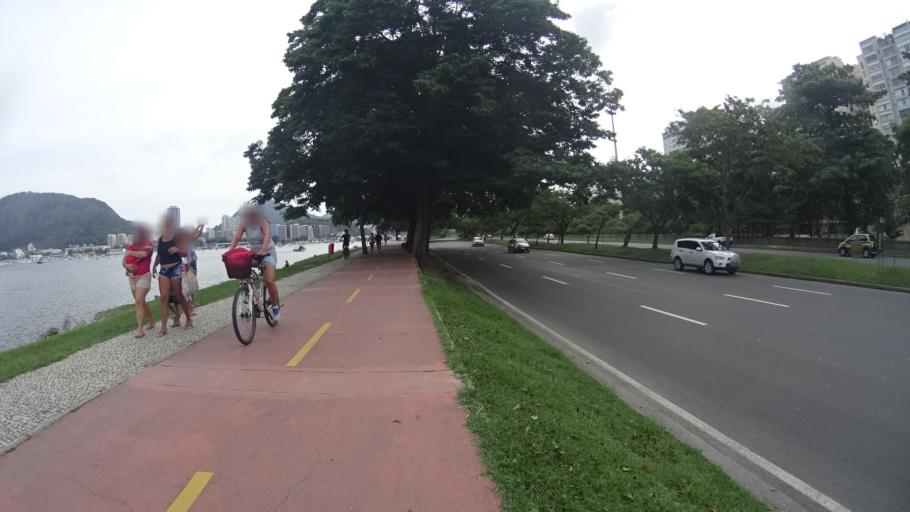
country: BR
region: Rio de Janeiro
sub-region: Rio De Janeiro
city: Rio de Janeiro
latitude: -22.9419
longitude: -43.1715
